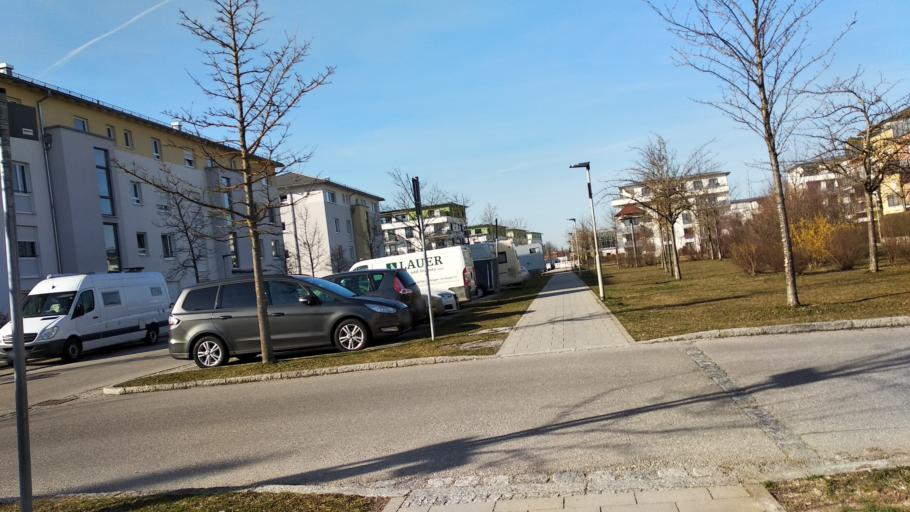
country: DE
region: Bavaria
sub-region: Upper Bavaria
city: Unterhaching
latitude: 48.0690
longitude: 11.6146
